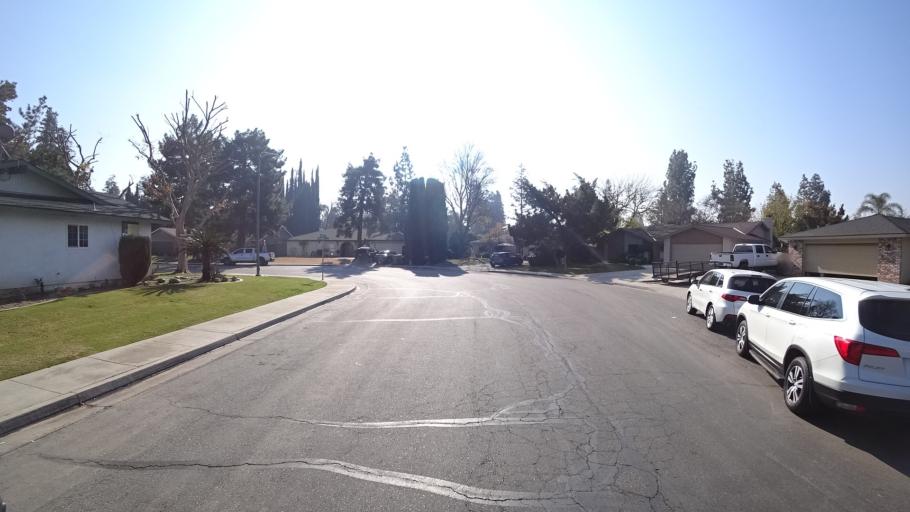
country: US
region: California
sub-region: Kern County
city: Greenacres
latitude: 35.3567
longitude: -119.0773
